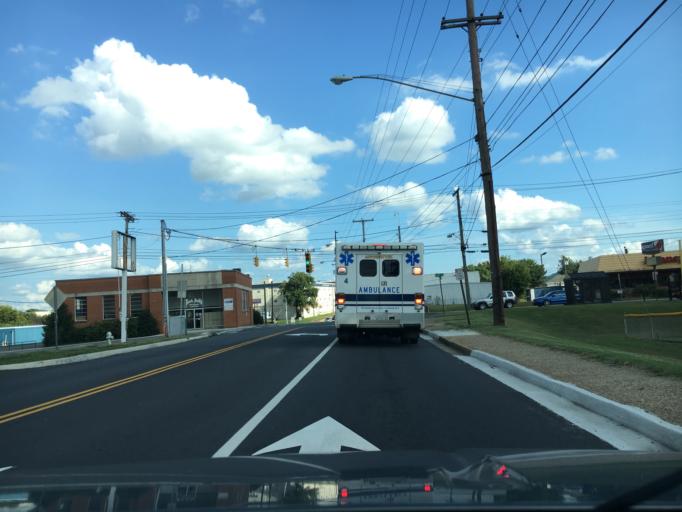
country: US
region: Virginia
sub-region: City of Lynchburg
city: West Lynchburg
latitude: 37.4036
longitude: -79.1591
